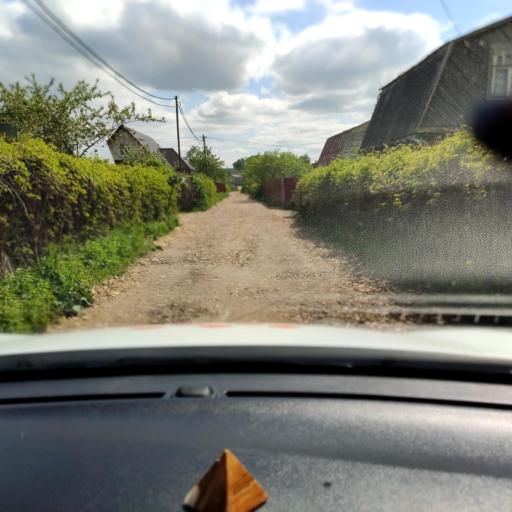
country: RU
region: Tatarstan
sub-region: Gorod Kazan'
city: Kazan
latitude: 55.8602
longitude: 49.1875
